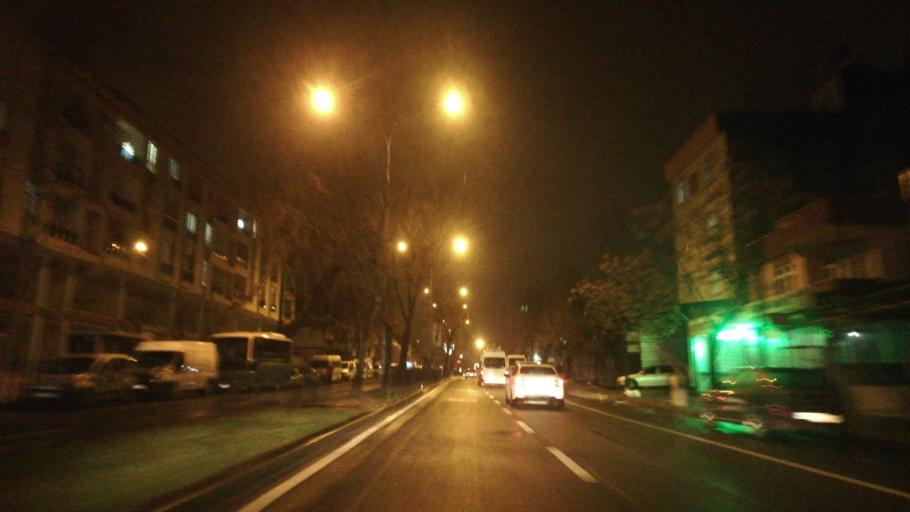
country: TR
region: Kahramanmaras
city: Kahramanmaras
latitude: 37.5726
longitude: 36.8975
